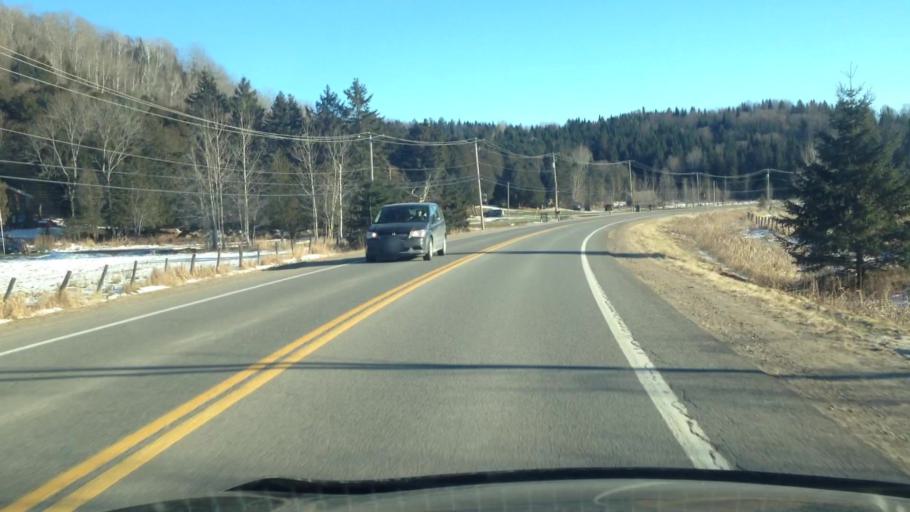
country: CA
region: Quebec
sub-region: Laurentides
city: Mont-Tremblant
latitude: 45.9588
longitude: -74.5698
